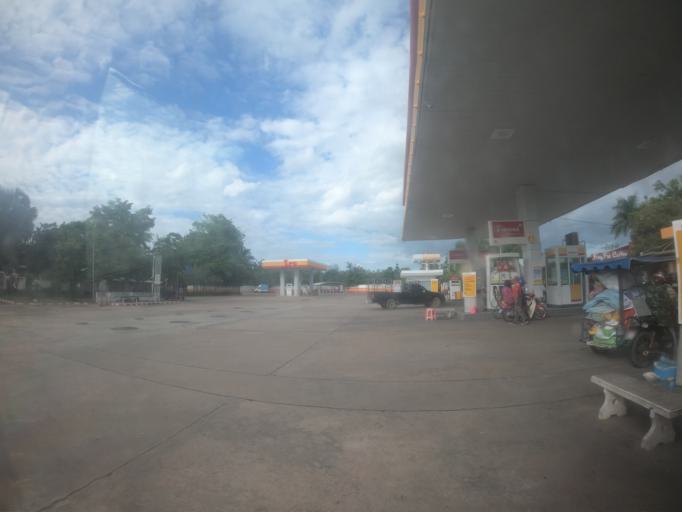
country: TH
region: Surin
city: Prasat
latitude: 14.6225
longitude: 103.4120
